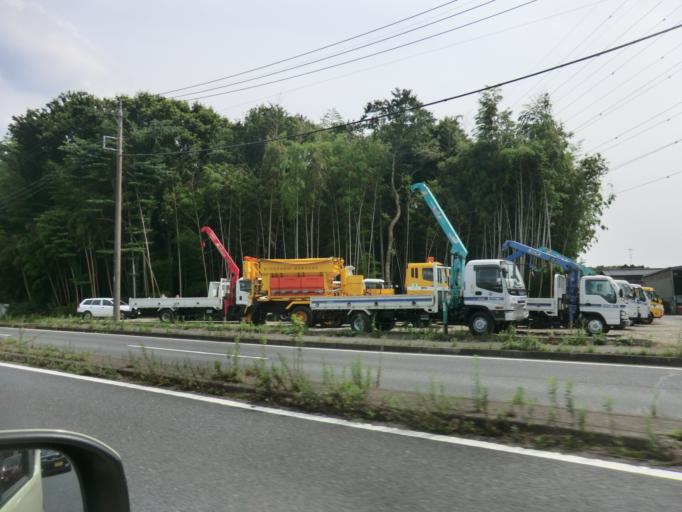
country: JP
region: Chiba
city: Noda
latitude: 35.9240
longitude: 139.9162
